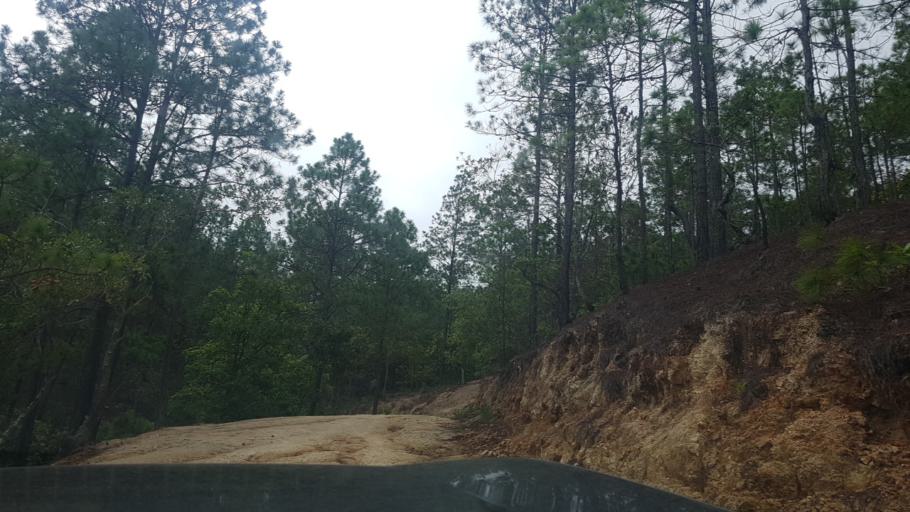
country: NI
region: Madriz
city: Totogalpa
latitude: 13.6143
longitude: -86.6103
